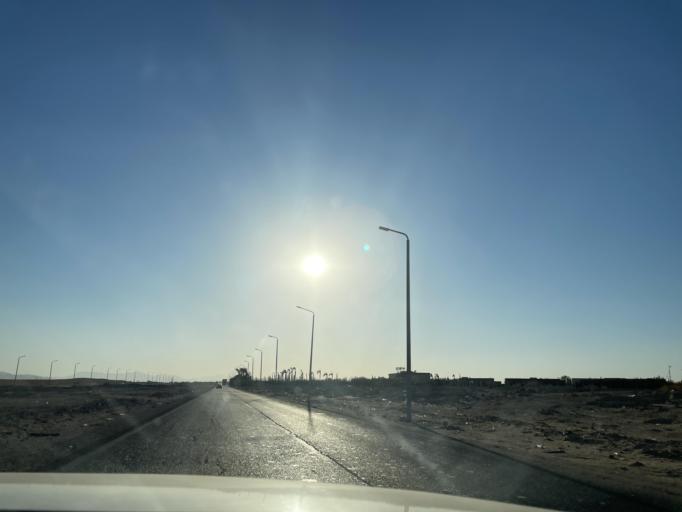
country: EG
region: Red Sea
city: Hurghada
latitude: 27.2175
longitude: 33.7979
